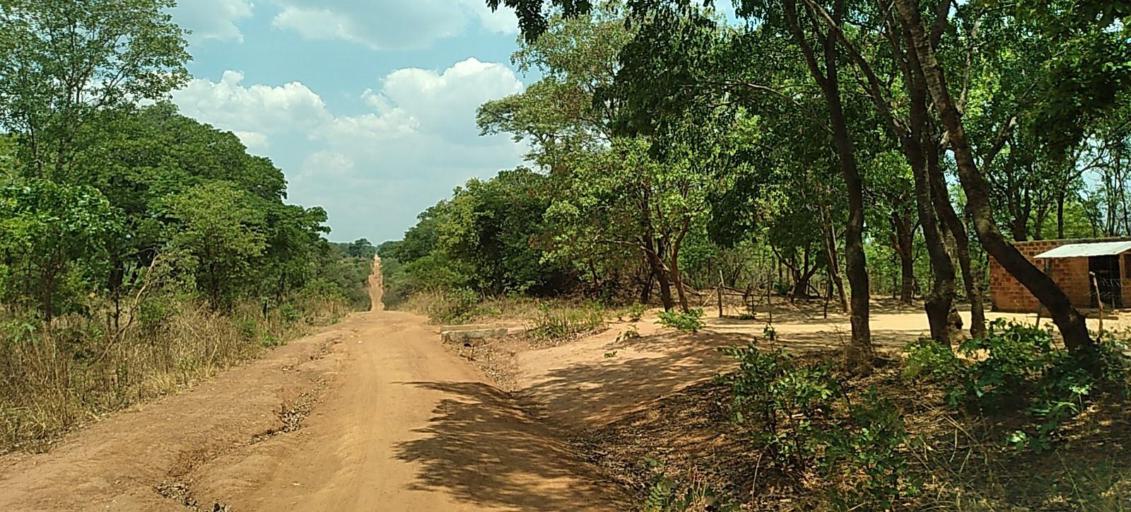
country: ZM
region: Copperbelt
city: Luanshya
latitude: -13.3892
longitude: 28.4478
